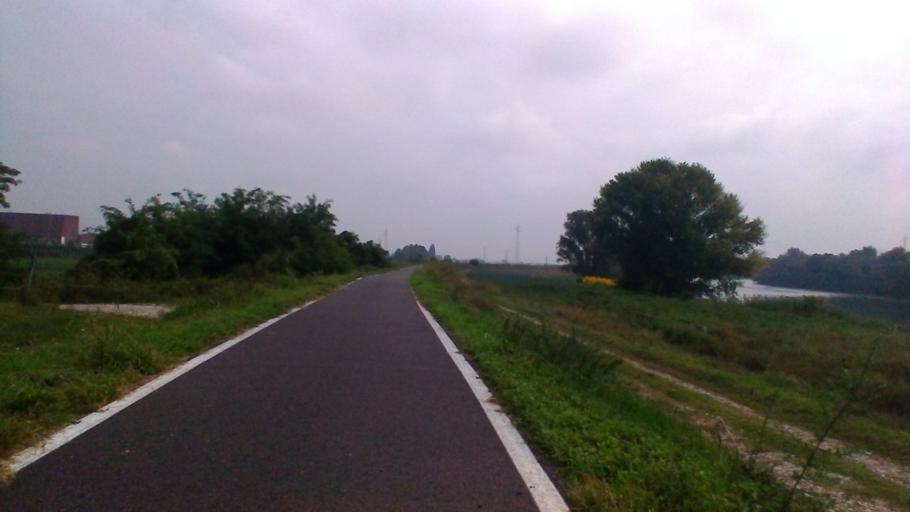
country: IT
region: Veneto
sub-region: Provincia di Verona
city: San Giovanni Lupatoto
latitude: 45.3974
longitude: 11.0466
